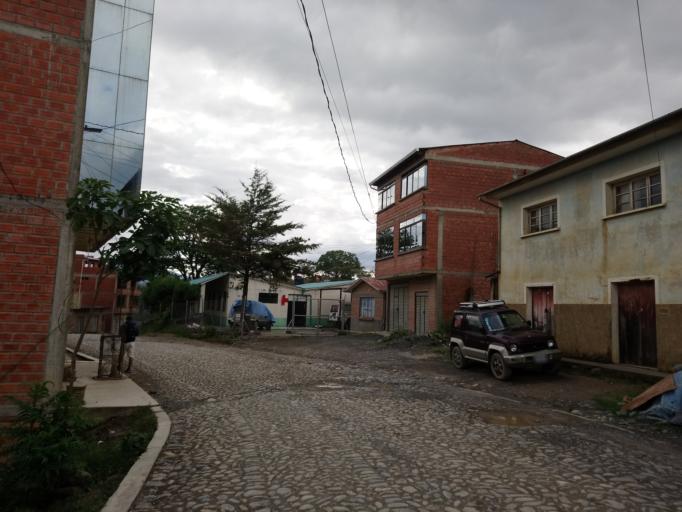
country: BO
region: La Paz
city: Coripata
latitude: -16.2702
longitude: -67.6386
